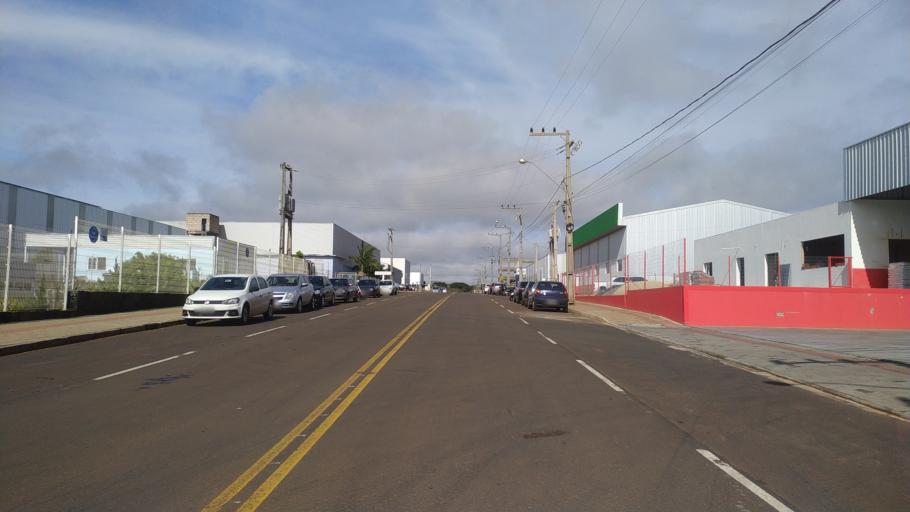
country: BR
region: Santa Catarina
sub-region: Chapeco
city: Chapeco
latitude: -27.1575
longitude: -52.6004
